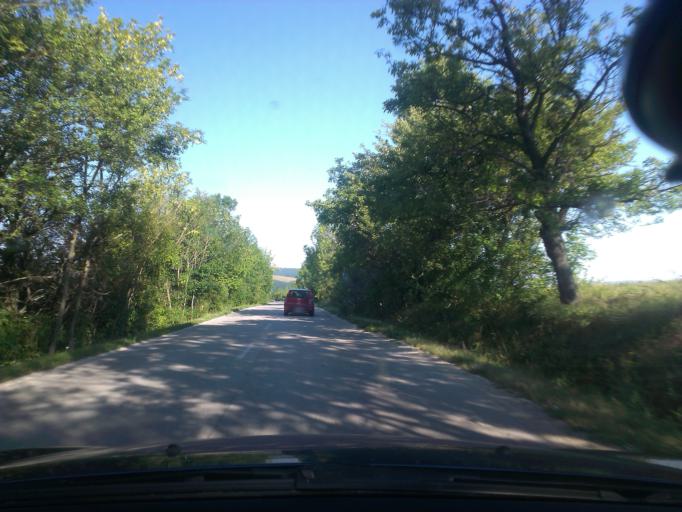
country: SK
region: Trnavsky
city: Vrbove
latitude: 48.6816
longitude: 17.6879
